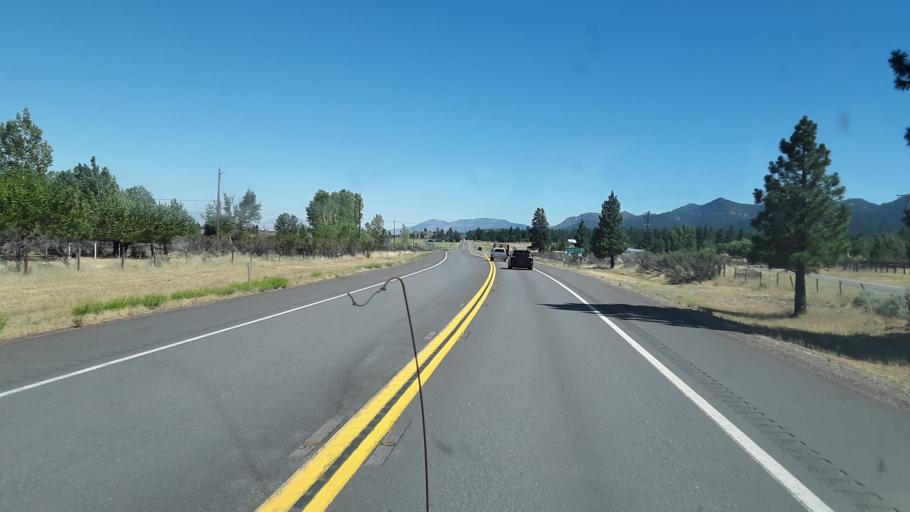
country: US
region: California
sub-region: Lassen County
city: Janesville
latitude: 40.3169
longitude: -120.5418
